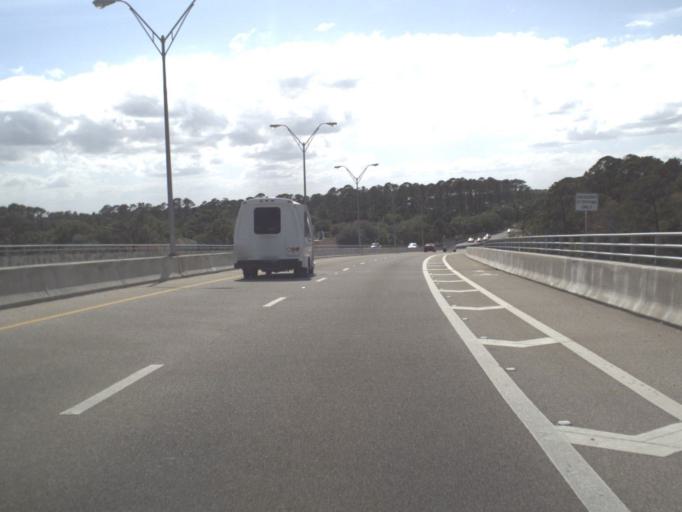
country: US
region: Florida
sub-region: Flagler County
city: Flagler Beach
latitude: 29.4770
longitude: -81.1387
